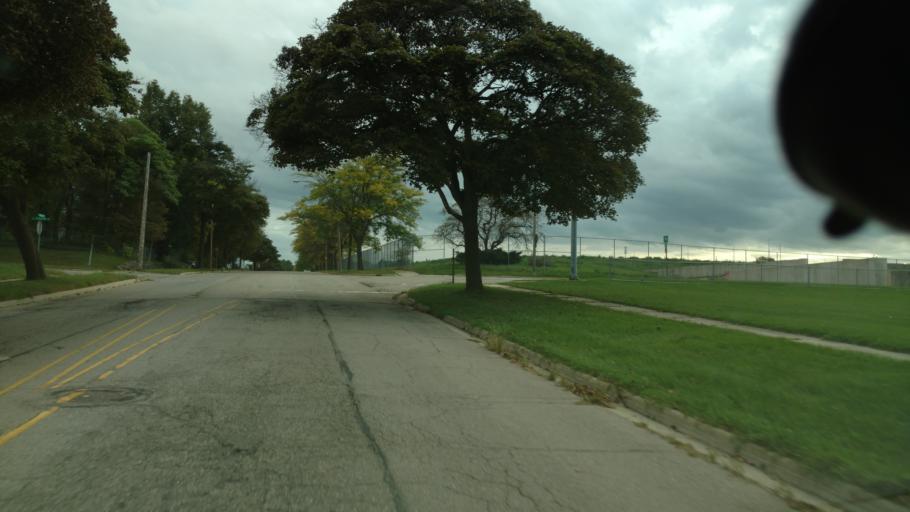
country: US
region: Michigan
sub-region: Ingham County
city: Edgemont Park
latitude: 42.7392
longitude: -84.5771
